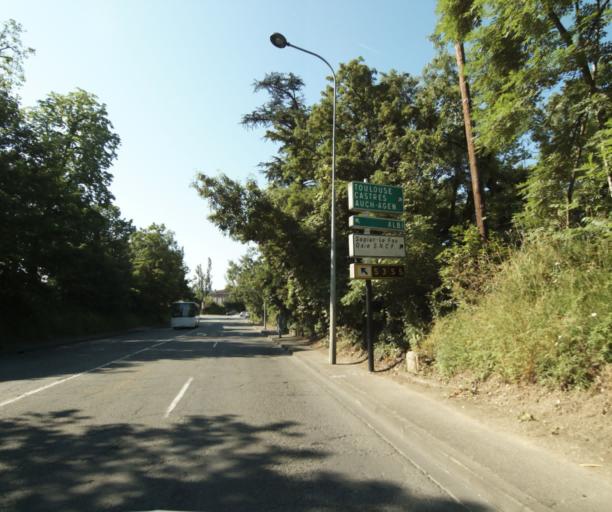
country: FR
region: Midi-Pyrenees
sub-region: Departement du Tarn-et-Garonne
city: Montauban
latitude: 44.0054
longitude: 1.3616
